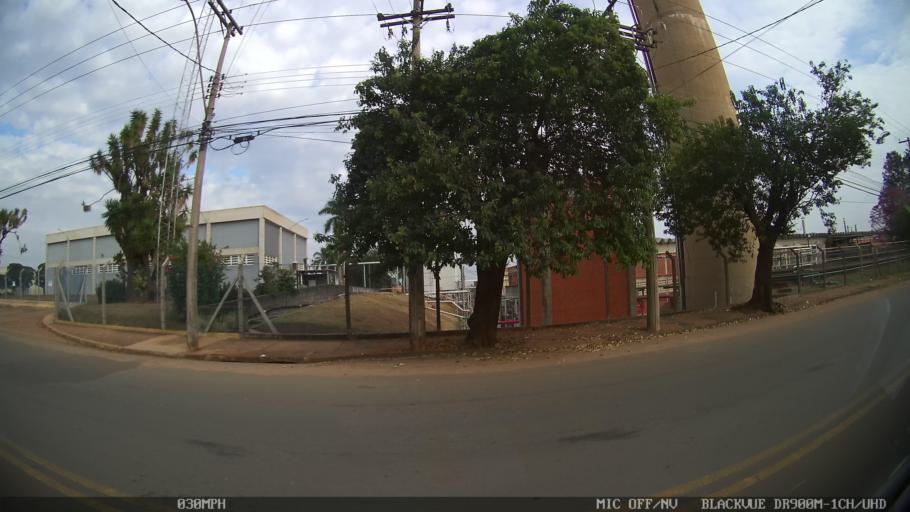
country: BR
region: Sao Paulo
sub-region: Santa Barbara D'Oeste
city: Santa Barbara d'Oeste
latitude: -22.7565
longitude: -47.3864
